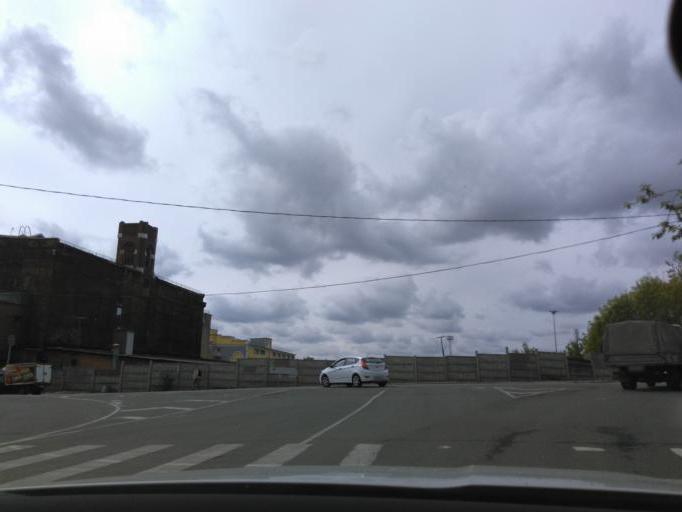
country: RU
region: Moscow
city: Zamoskvorech'ye
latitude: 55.7226
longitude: 37.6437
